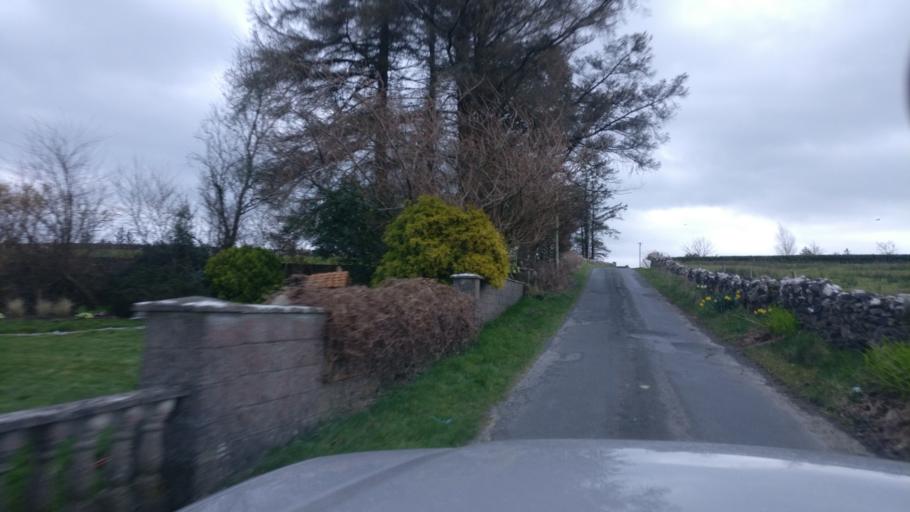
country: IE
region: Connaught
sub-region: County Galway
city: Loughrea
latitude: 53.2676
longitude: -8.4710
